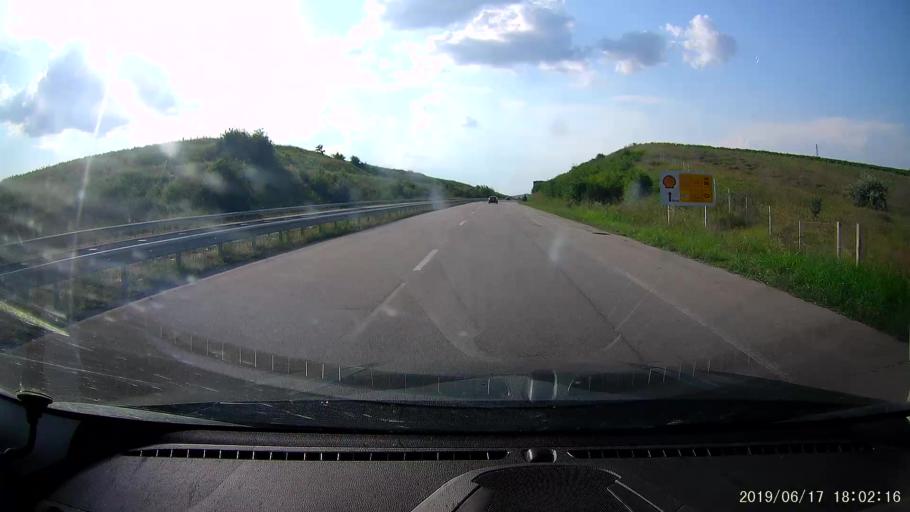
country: BG
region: Khaskovo
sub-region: Obshtina Svilengrad
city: Svilengrad
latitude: 41.7569
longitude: 26.2337
